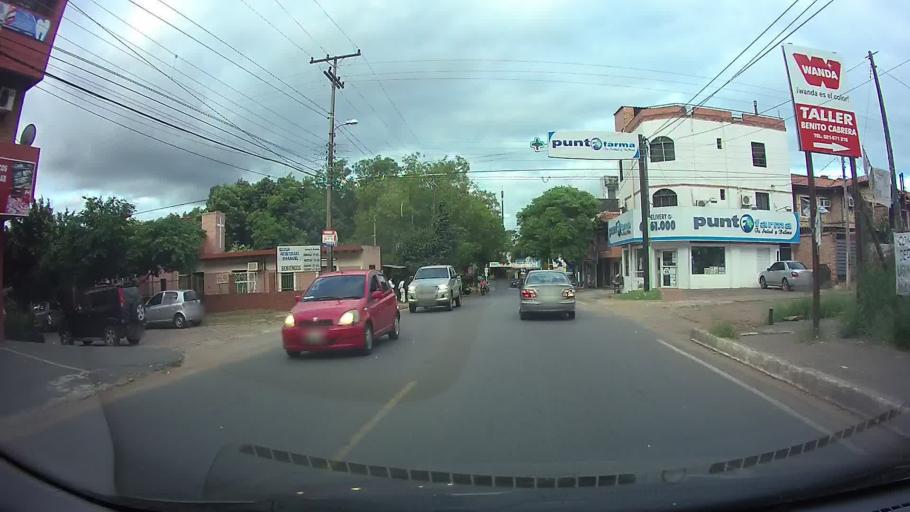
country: PY
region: Central
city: Fernando de la Mora
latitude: -25.3089
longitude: -57.5289
